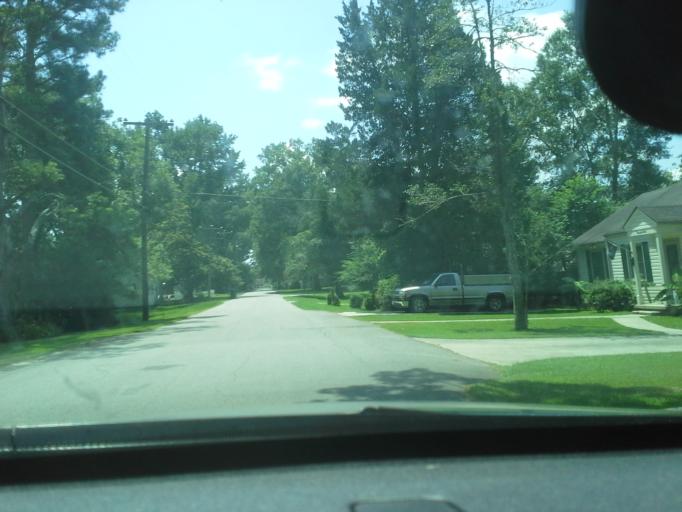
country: US
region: North Carolina
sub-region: Washington County
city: Plymouth
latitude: 35.8604
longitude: -76.7589
